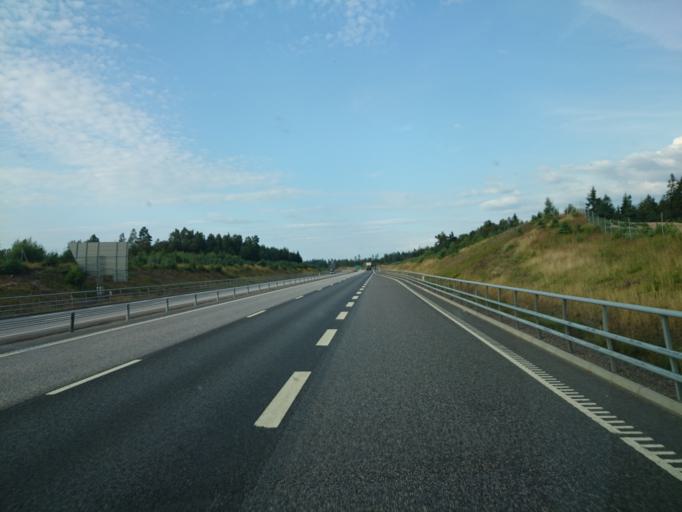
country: SE
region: Kronoberg
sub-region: Markaryds Kommun
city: Markaryd
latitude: 56.4712
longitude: 13.6382
